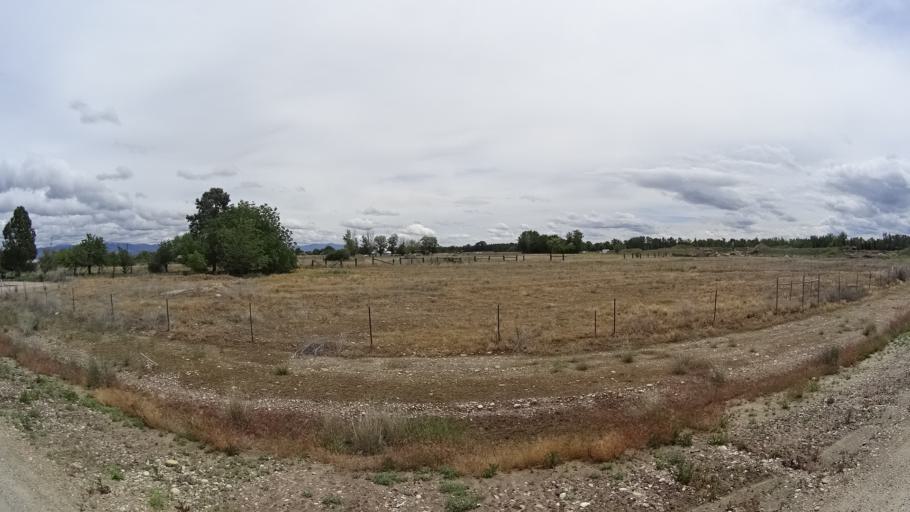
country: US
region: Idaho
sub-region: Ada County
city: Star
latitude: 43.6893
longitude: -116.4595
